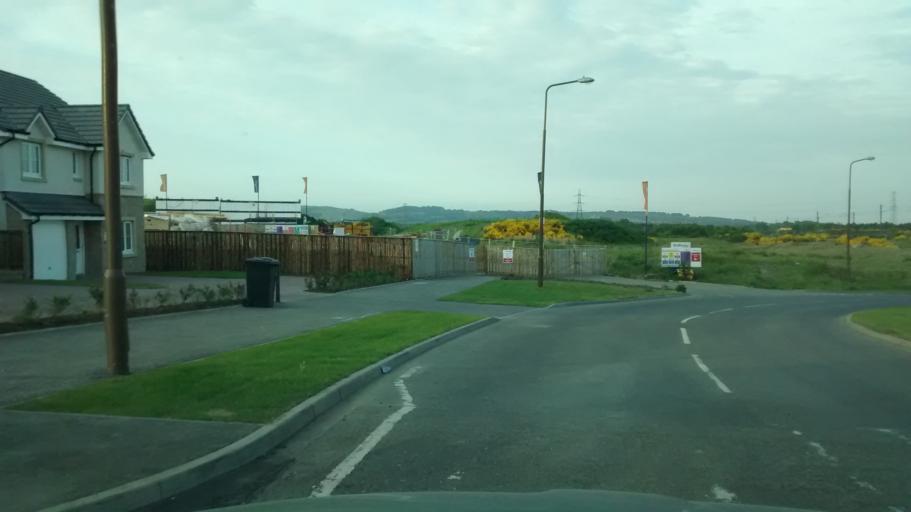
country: GB
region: Scotland
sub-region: West Lothian
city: Armadale
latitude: 55.8883
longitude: -3.6916
